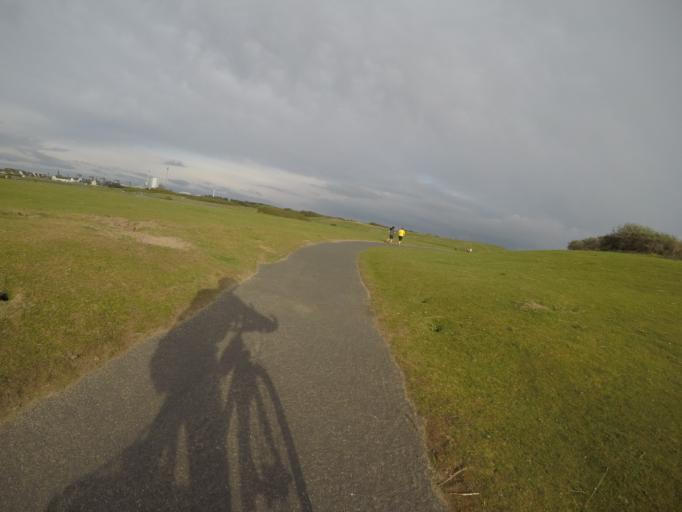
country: GB
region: Scotland
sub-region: North Ayrshire
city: Irvine
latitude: 55.6043
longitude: -4.6910
